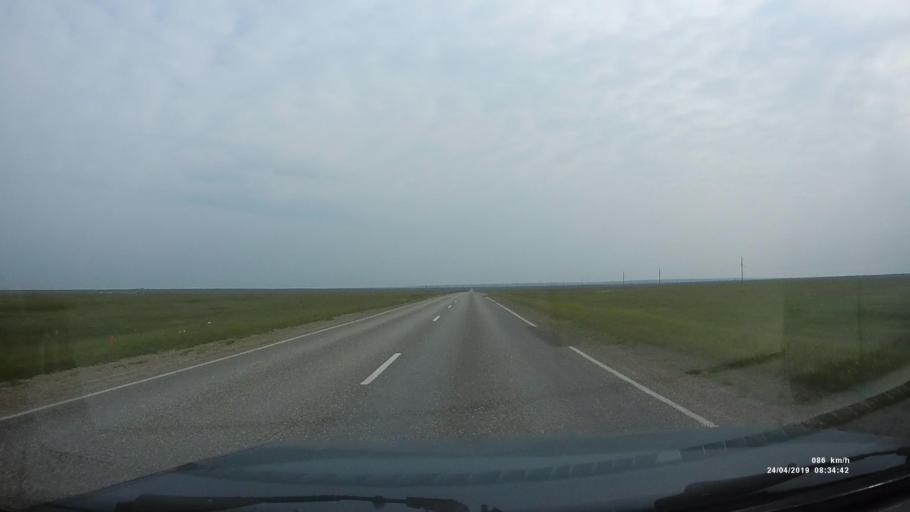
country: RU
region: Kalmykiya
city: Arshan'
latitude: 46.1922
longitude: 43.9085
